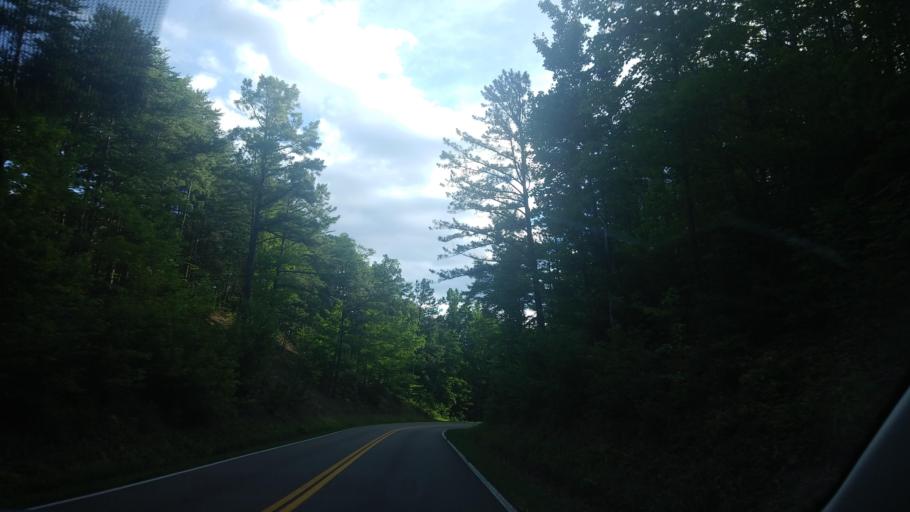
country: US
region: Tennessee
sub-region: Cocke County
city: Newport
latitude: 35.8179
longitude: -83.2182
